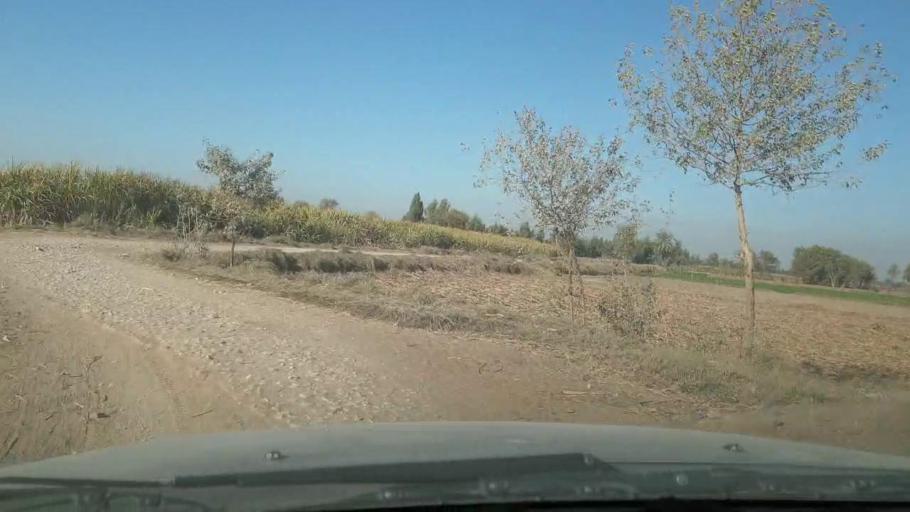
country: PK
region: Sindh
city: Adilpur
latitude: 27.9541
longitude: 69.1986
